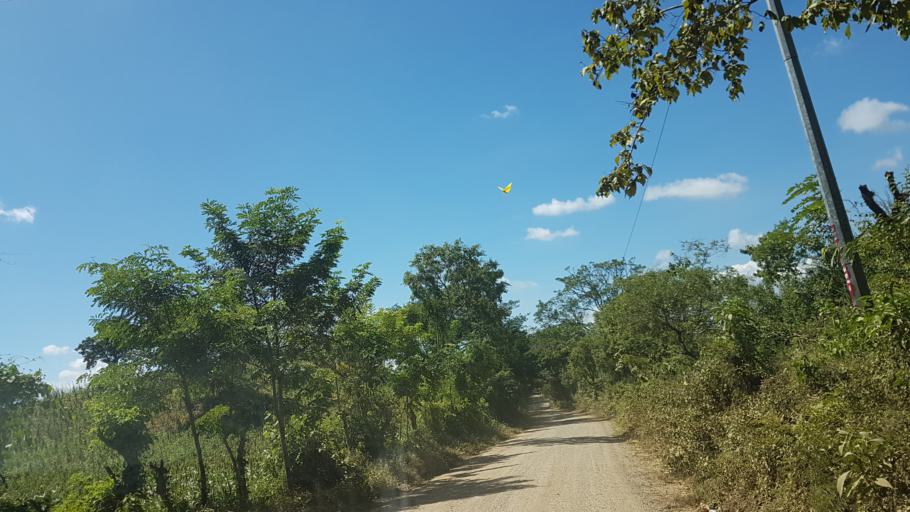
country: HN
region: El Paraiso
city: Santa Cruz
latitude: 13.7349
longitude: -86.6747
